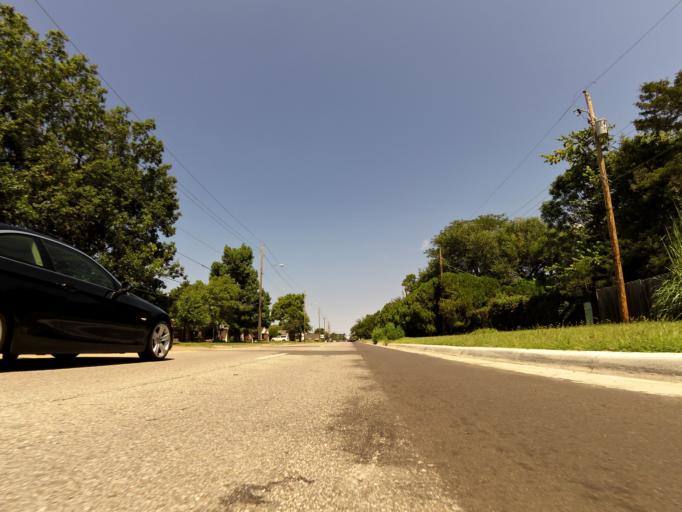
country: US
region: Kansas
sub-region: Sedgwick County
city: Bellaire
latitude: 37.6910
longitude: -97.2621
